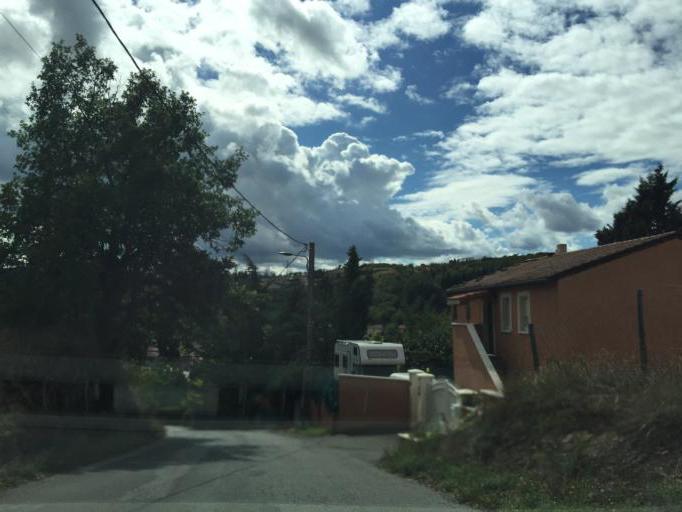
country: FR
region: Rhone-Alpes
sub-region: Departement de la Loire
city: Saint-Martin-la-Plaine
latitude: 45.5266
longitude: 4.5840
